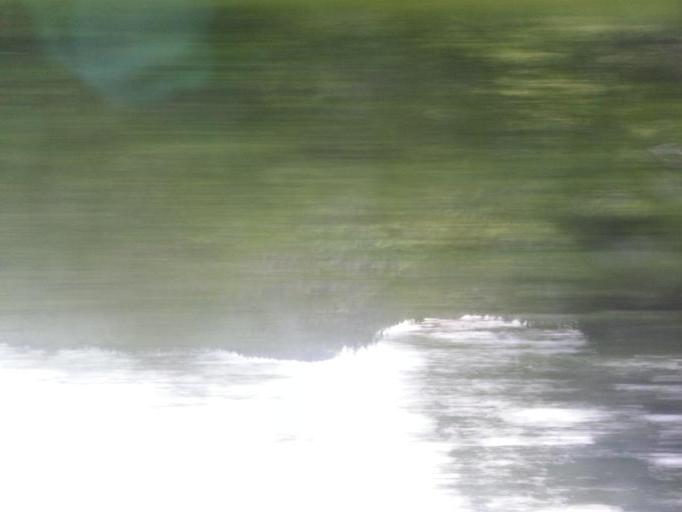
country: NO
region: Sor-Trondelag
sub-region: Midtre Gauldal
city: Storen
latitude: 62.9849
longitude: 10.2347
